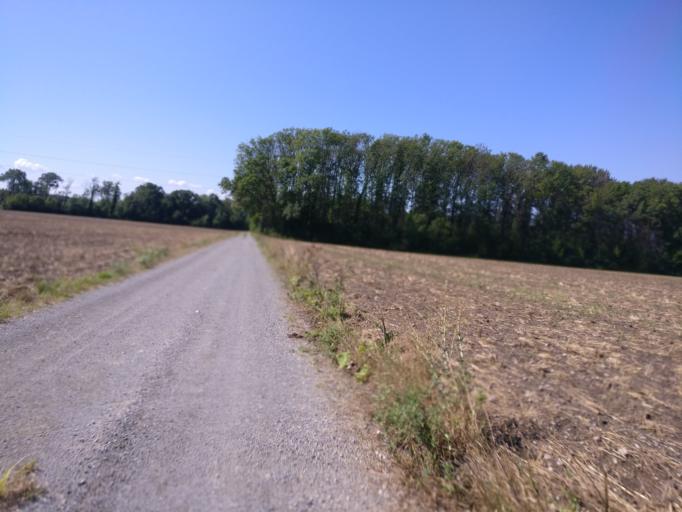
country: AT
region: Lower Austria
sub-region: Politischer Bezirk Baden
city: Pottendorf
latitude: 47.9282
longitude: 16.3687
